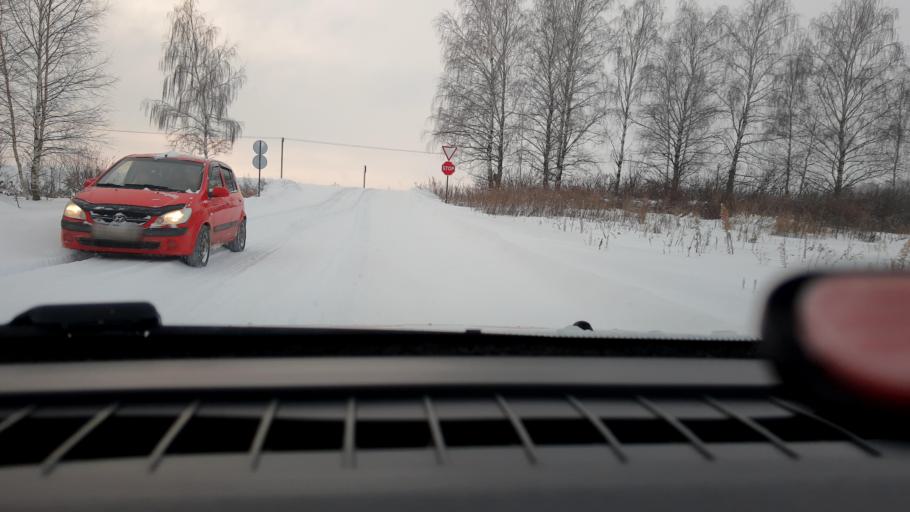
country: RU
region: Nizjnij Novgorod
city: Burevestnik
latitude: 56.1278
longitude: 43.9533
